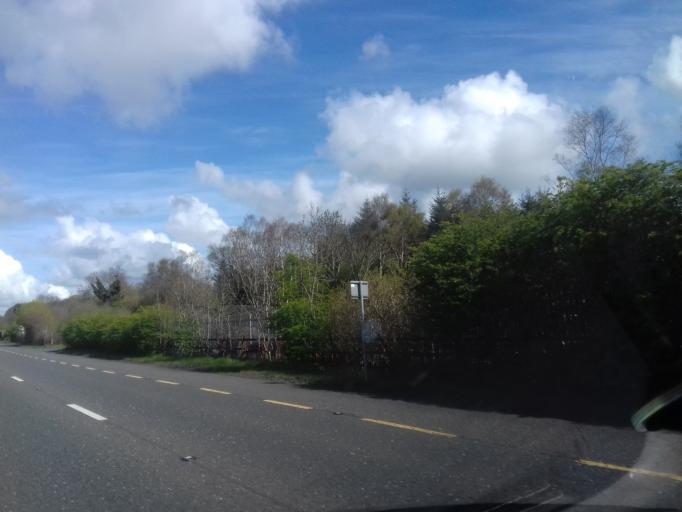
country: IE
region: Ulster
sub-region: An Cabhan
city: Cavan
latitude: 54.0538
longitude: -7.3853
